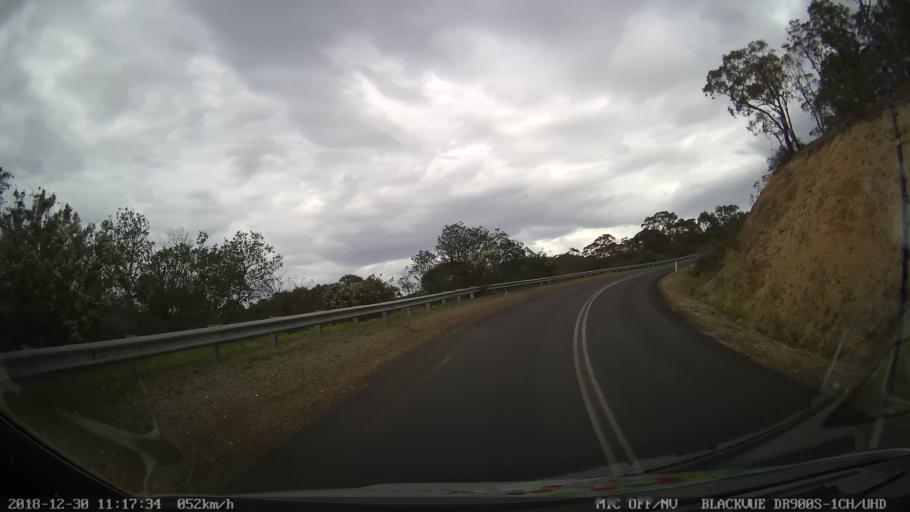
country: AU
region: New South Wales
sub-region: Snowy River
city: Jindabyne
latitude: -36.5370
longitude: 148.6973
